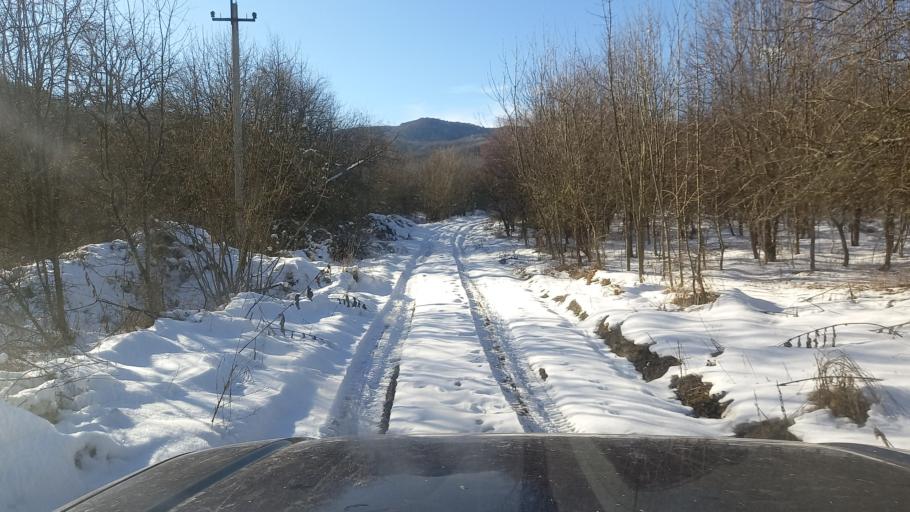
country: RU
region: Adygeya
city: Kamennomostskiy
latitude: 44.2053
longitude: 40.1455
